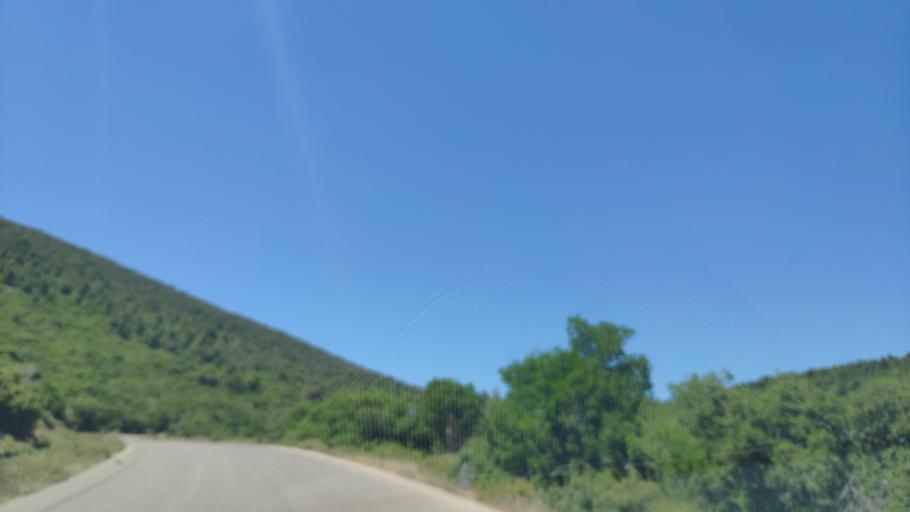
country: GR
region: Central Greece
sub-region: Nomos Voiotias
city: Kaparellion
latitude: 38.2066
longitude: 23.1747
